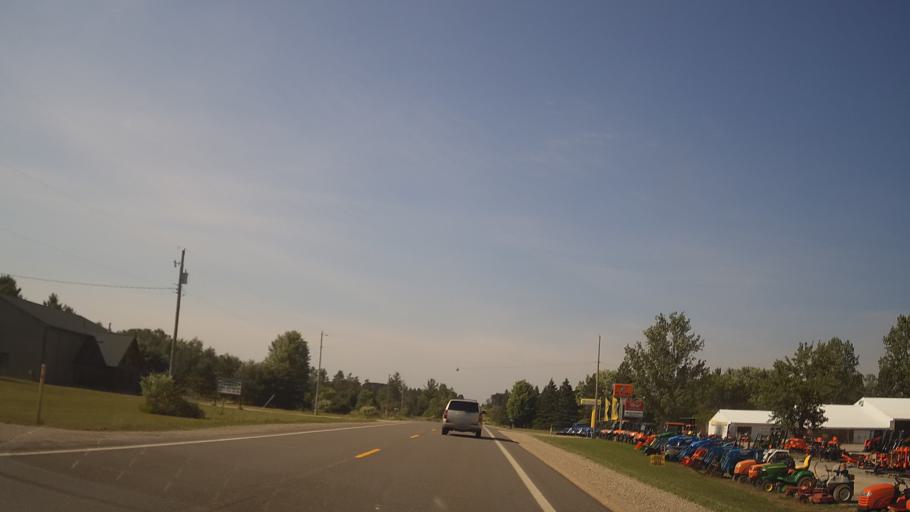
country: US
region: Michigan
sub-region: Ogemaw County
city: West Branch
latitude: 44.3280
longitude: -84.1257
